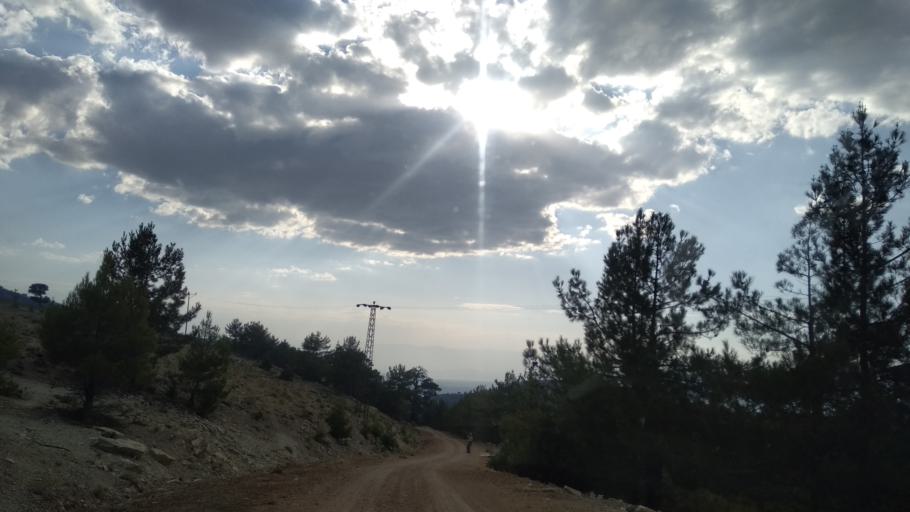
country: TR
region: Mersin
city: Sarikavak
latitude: 36.6010
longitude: 33.7213
